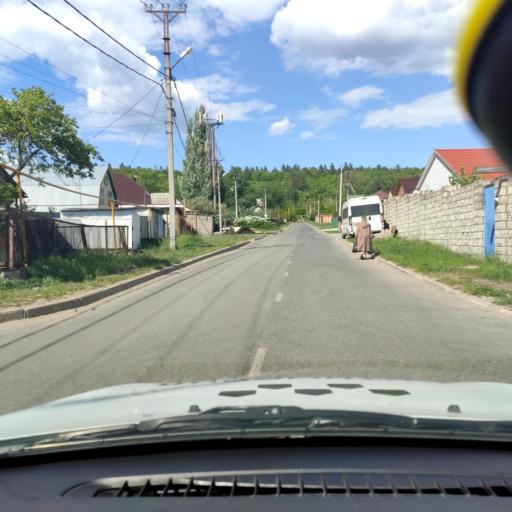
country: RU
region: Samara
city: Zhigulevsk
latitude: 53.4682
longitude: 49.6316
